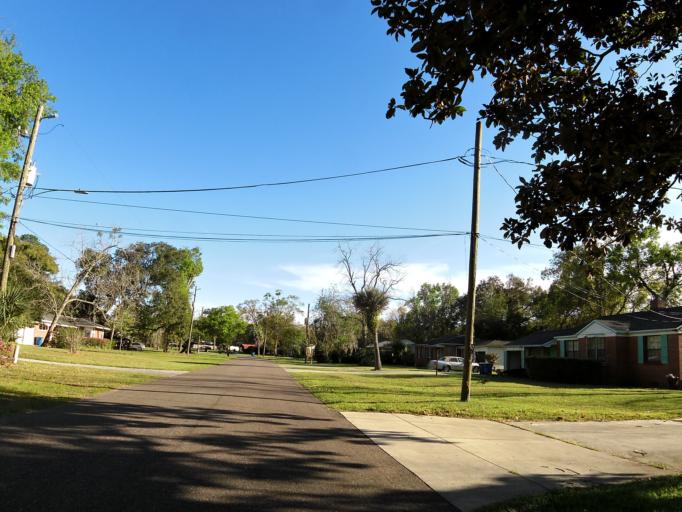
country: US
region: Florida
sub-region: Duval County
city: Jacksonville
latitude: 30.4020
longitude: -81.6720
